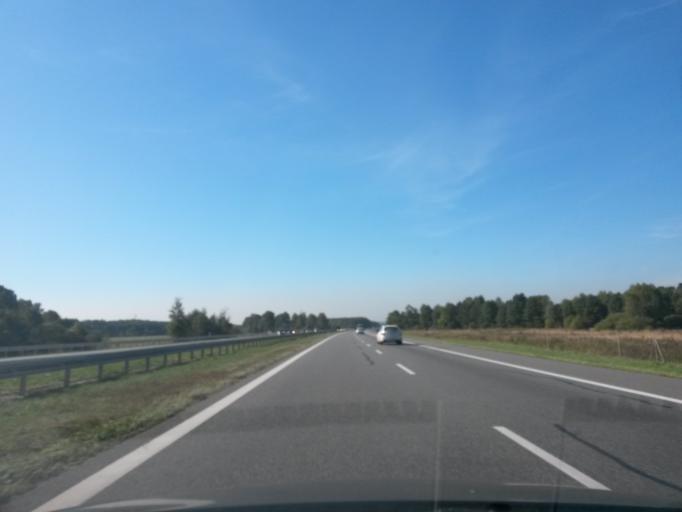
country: PL
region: Lesser Poland Voivodeship
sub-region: Powiat chrzanowski
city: Libiaz
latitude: 50.1479
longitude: 19.3112
